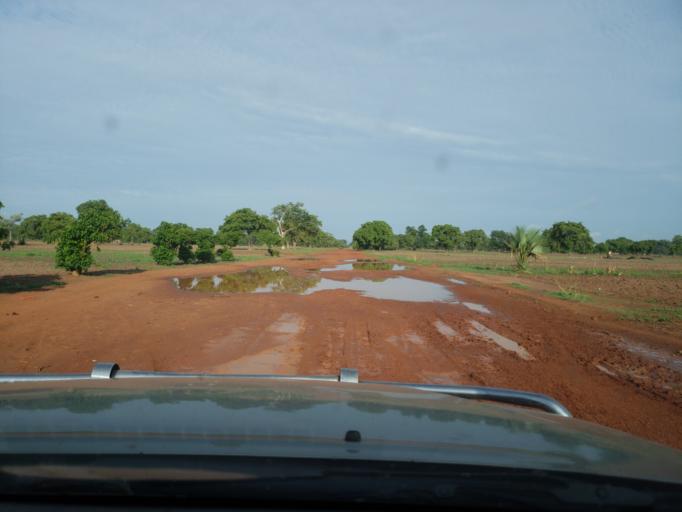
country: ML
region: Sikasso
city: Koutiala
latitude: 12.4202
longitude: -5.6966
